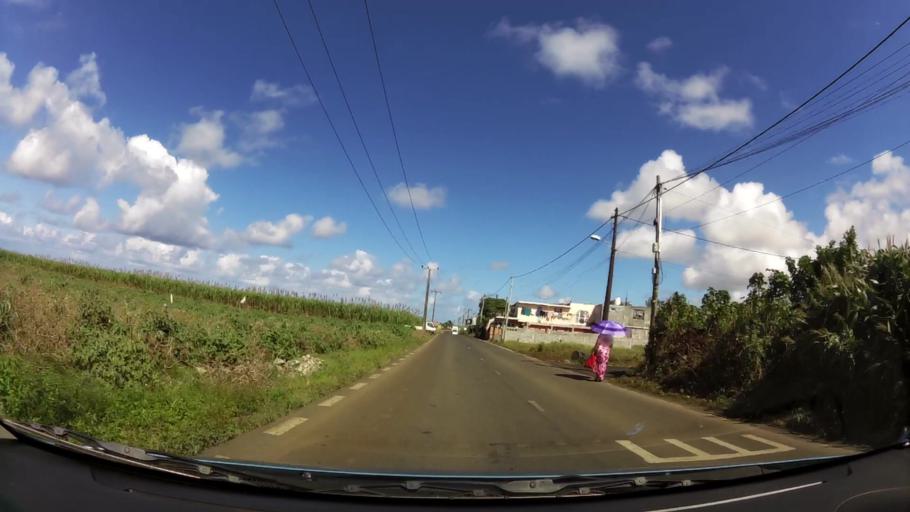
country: MU
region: Grand Port
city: Plaine Magnien
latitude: -20.4372
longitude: 57.6573
